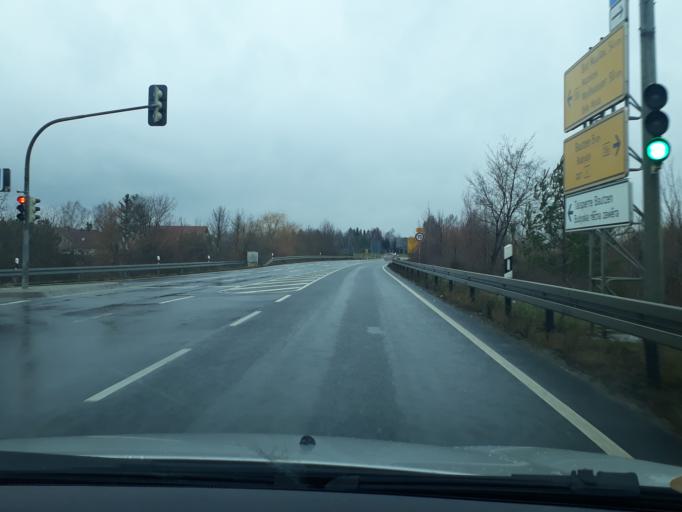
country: DE
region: Saxony
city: Bautzen
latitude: 51.1967
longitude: 14.4656
